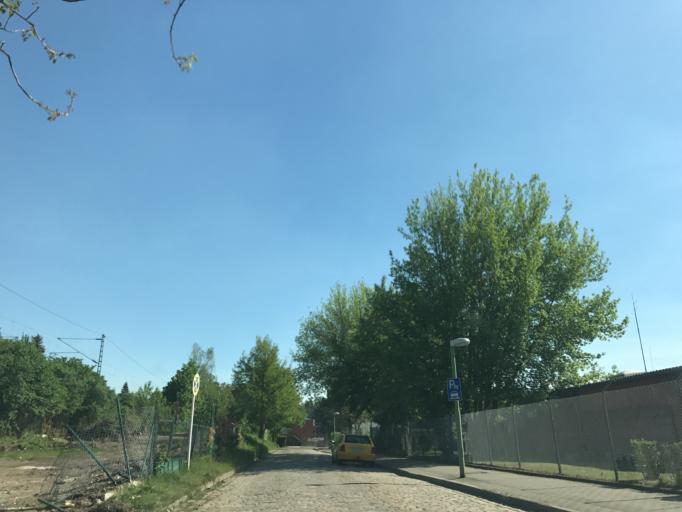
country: DE
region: Berlin
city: Siemensstadt
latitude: 52.5191
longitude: 13.2524
